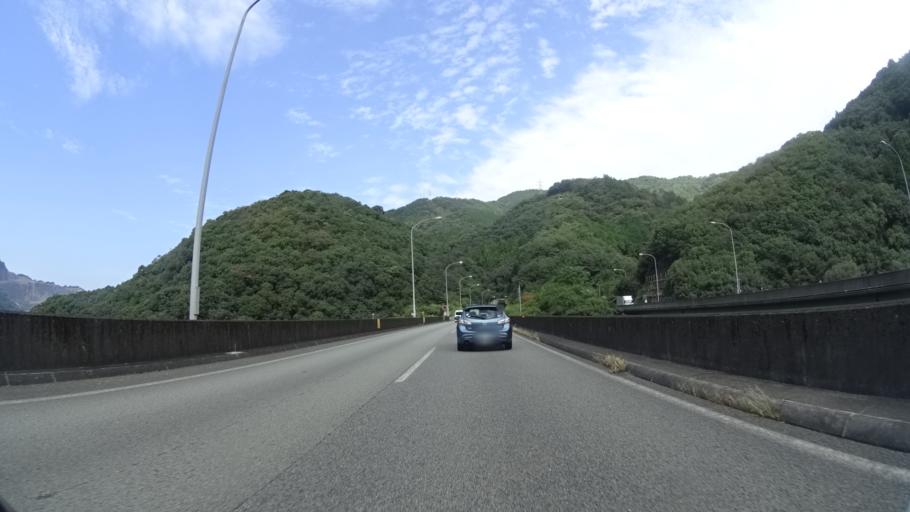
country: JP
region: Kumamoto
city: Yatsushiro
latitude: 32.4668
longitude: 130.6497
